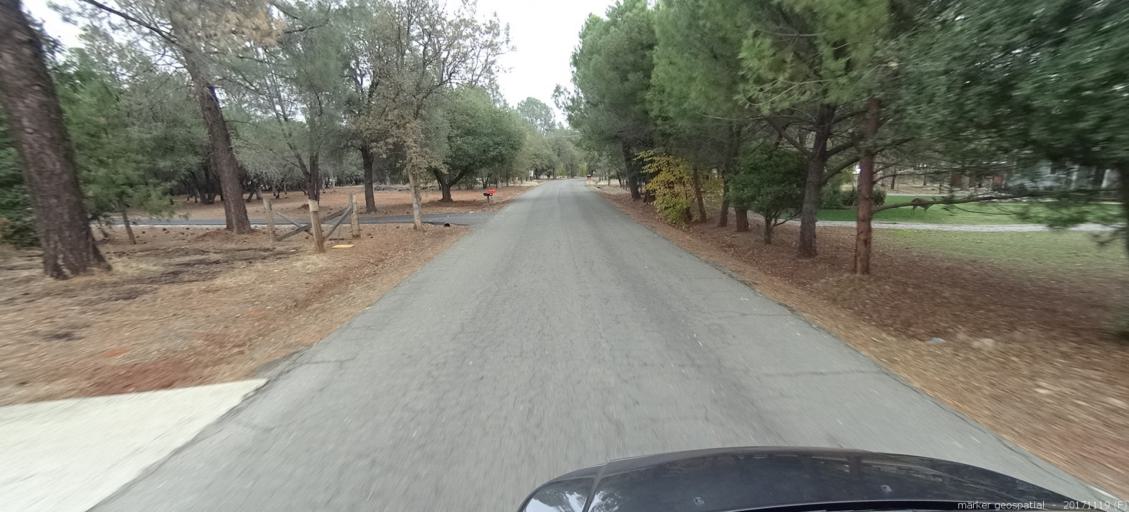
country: US
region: California
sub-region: Shasta County
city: Shasta
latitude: 40.4846
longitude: -122.4588
